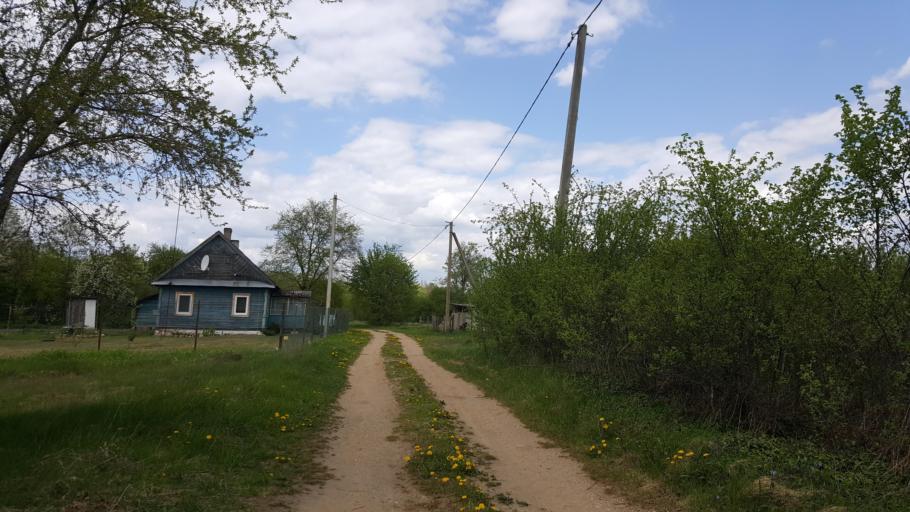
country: BY
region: Brest
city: Zhabinka
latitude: 52.3947
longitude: 24.0962
